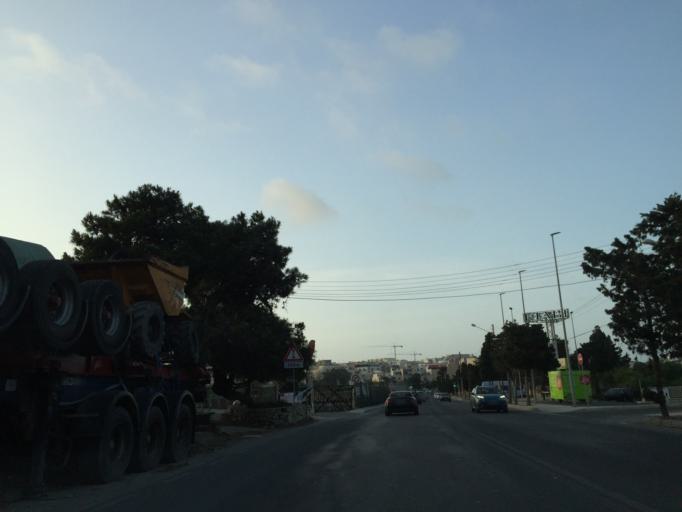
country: MT
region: Saint Paul's Bay
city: San Pawl il-Bahar
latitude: 35.9408
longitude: 14.4115
